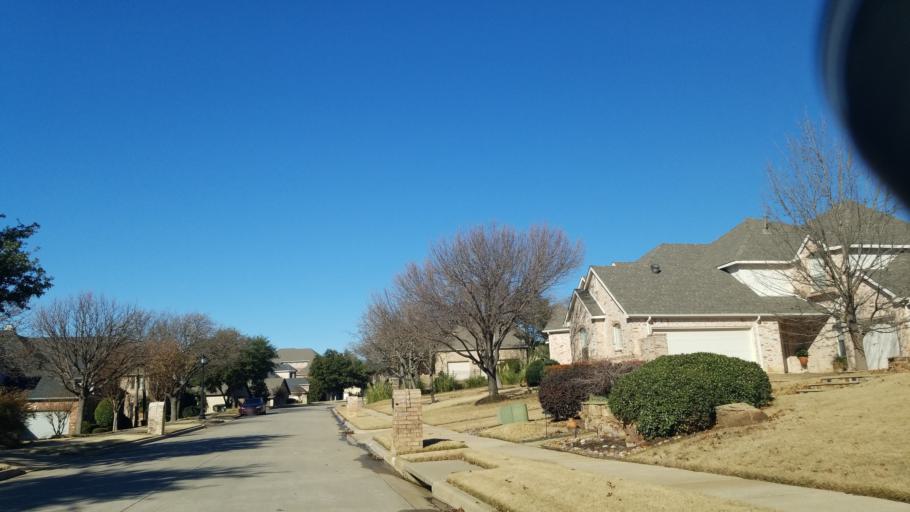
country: US
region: Texas
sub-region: Denton County
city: Corinth
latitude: 33.1528
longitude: -97.0881
